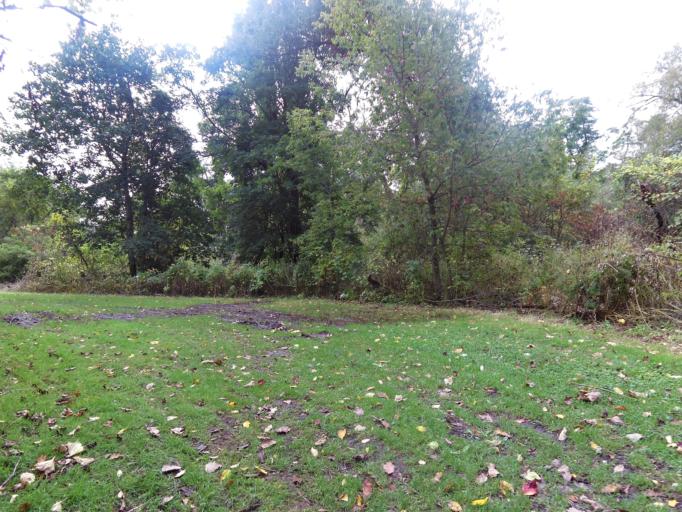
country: CA
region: Ontario
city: Scarborough
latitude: 43.7590
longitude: -79.1763
